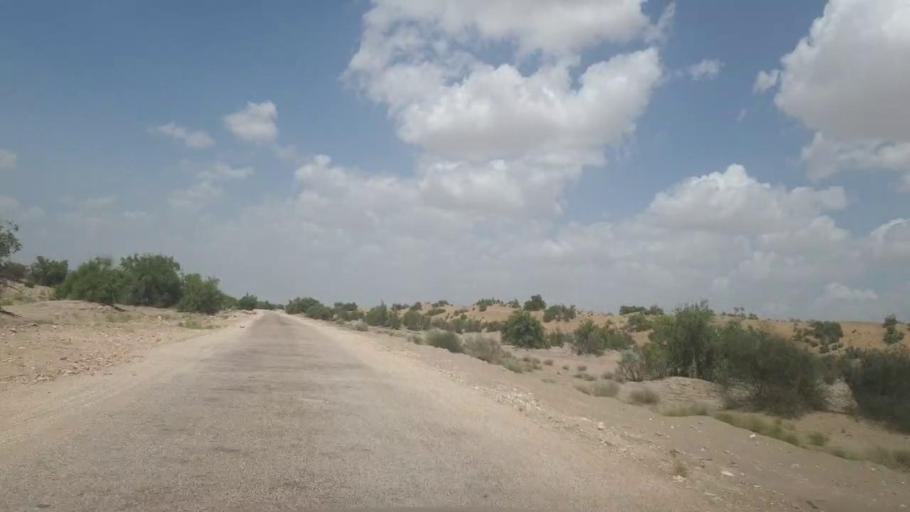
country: PK
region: Sindh
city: Kot Diji
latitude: 27.2530
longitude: 69.1639
